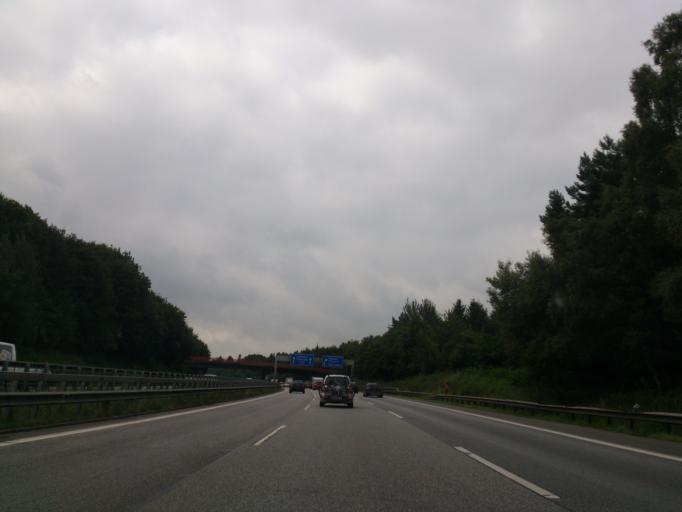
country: DE
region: Hamburg
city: Harburg
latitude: 53.4511
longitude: 9.9207
